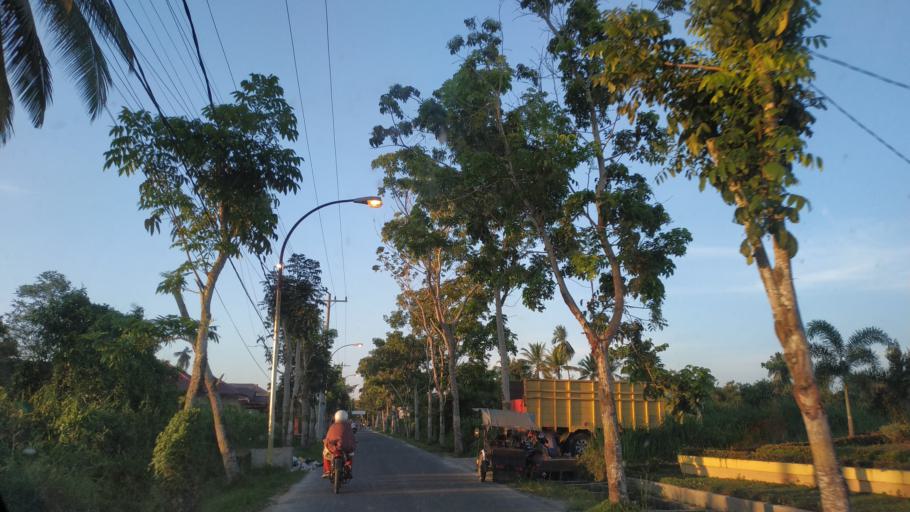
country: ID
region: North Sumatra
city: Tanjungbalai
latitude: 2.9438
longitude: 99.7880
